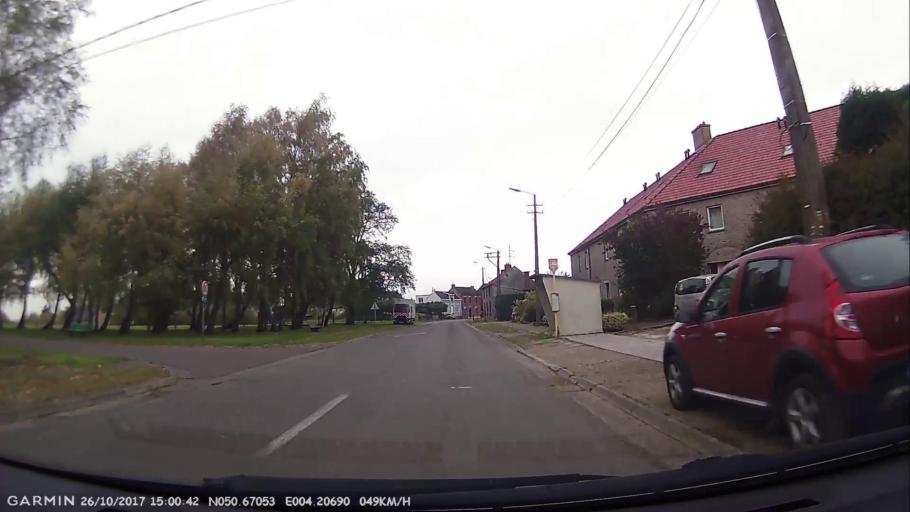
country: BE
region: Wallonia
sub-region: Province du Brabant Wallon
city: Tubize
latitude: 50.6709
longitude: 4.2067
